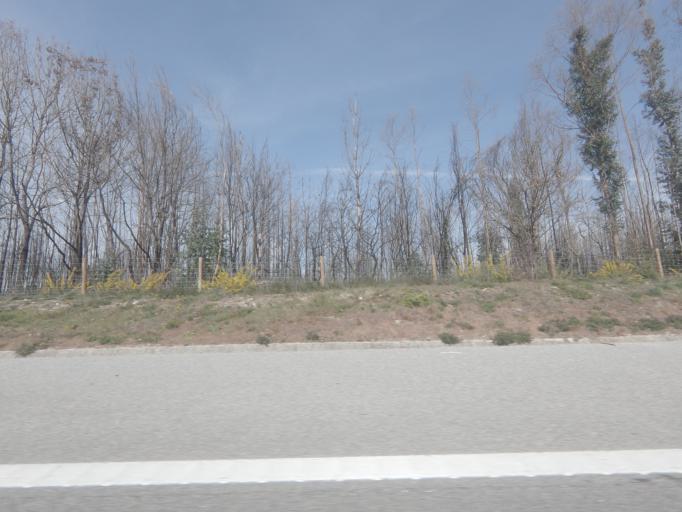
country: PT
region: Viseu
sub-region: Oliveira de Frades
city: Oliveira de Frades
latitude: 40.6862
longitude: -8.2107
